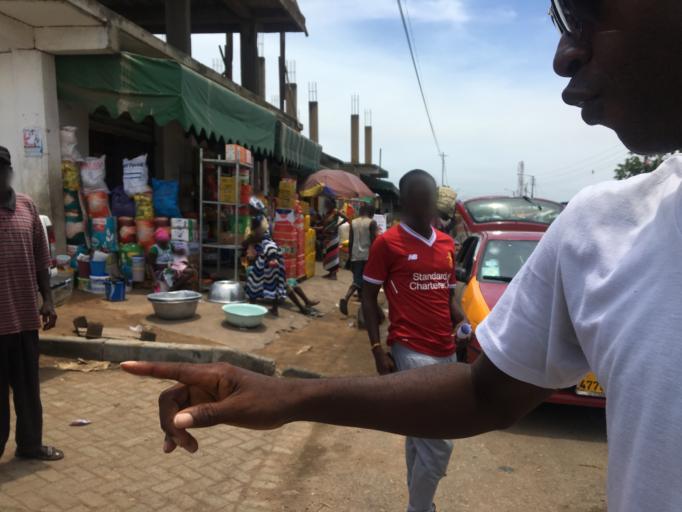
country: GH
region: Greater Accra
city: Accra
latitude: 5.5802
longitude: -0.1978
